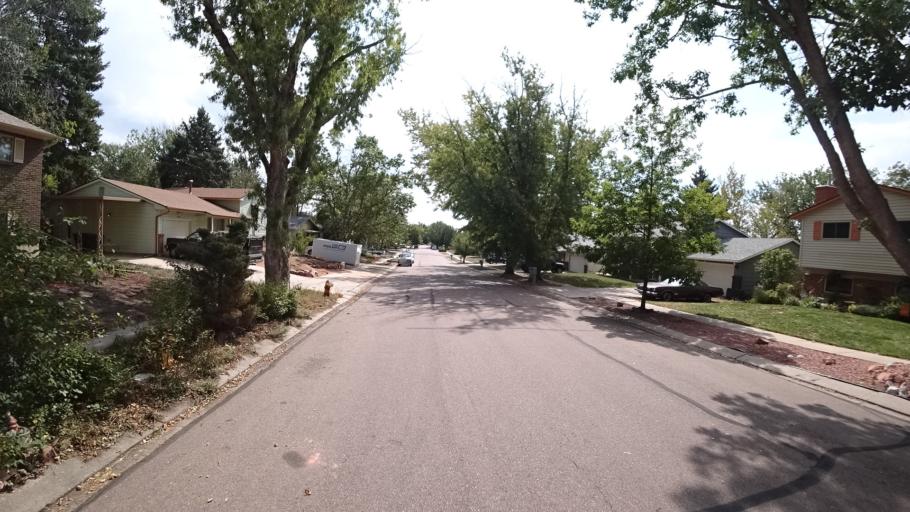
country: US
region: Colorado
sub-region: El Paso County
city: Cimarron Hills
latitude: 38.8527
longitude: -104.7439
